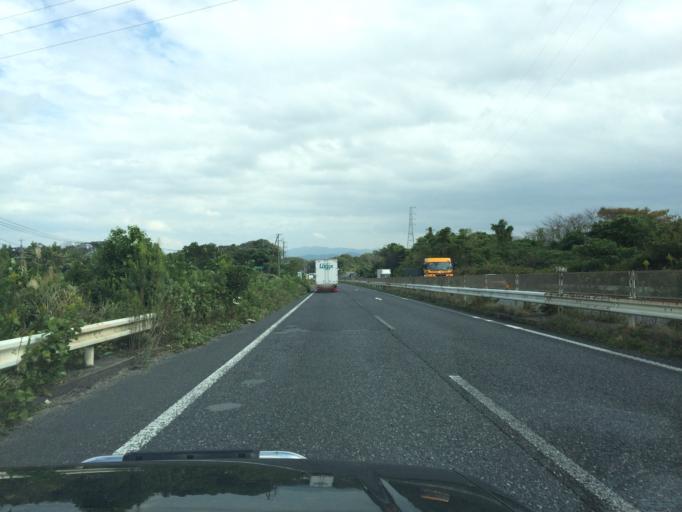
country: JP
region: Mie
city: Ueno-ebisumachi
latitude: 34.7256
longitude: 136.0891
